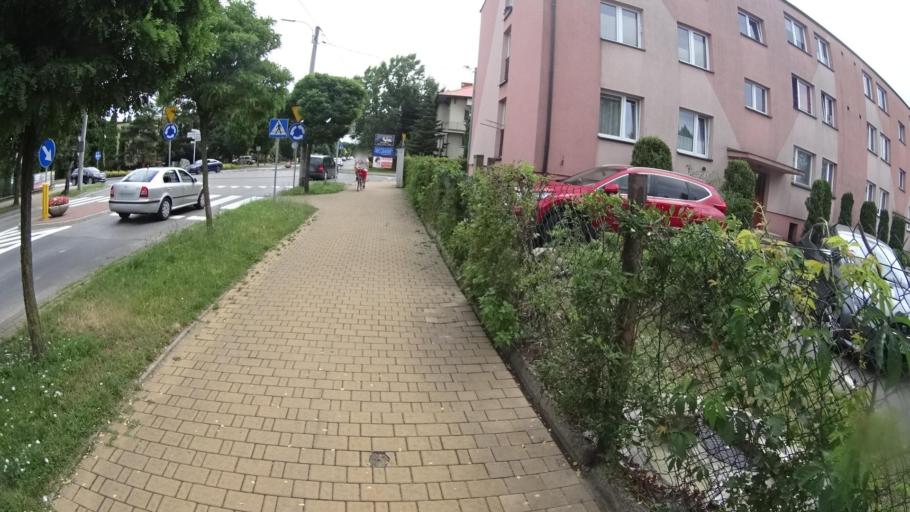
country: PL
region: Masovian Voivodeship
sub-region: Powiat grojecki
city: Grojec
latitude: 51.8604
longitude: 20.8682
